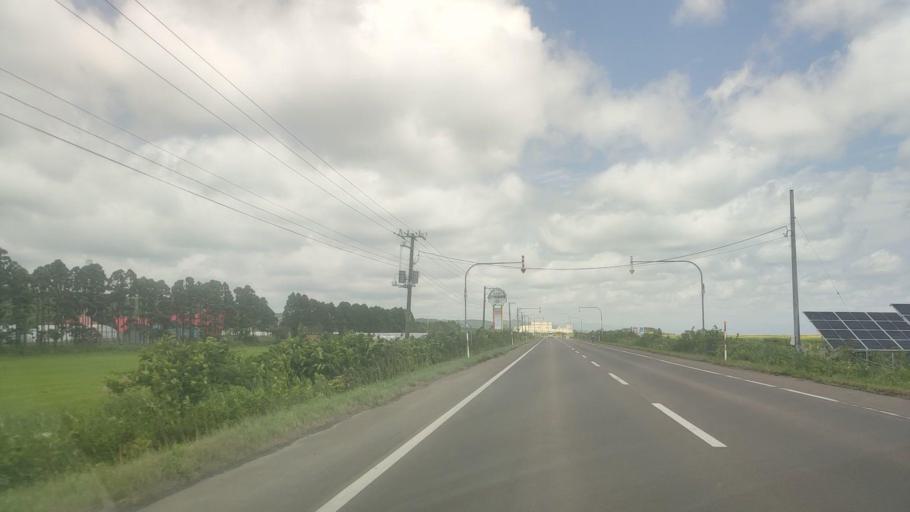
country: JP
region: Hokkaido
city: Niseko Town
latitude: 42.3782
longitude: 140.2925
